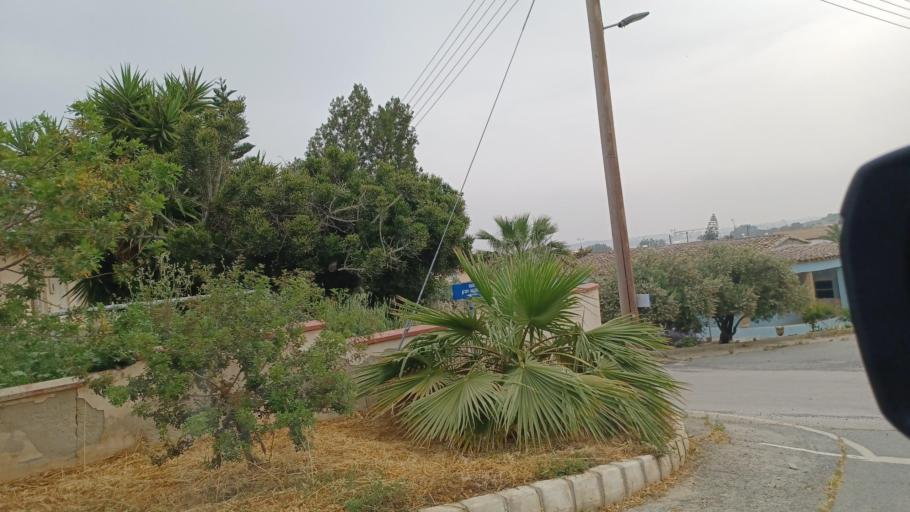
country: CY
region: Lefkosia
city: Mammari
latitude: 35.1757
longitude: 33.2024
